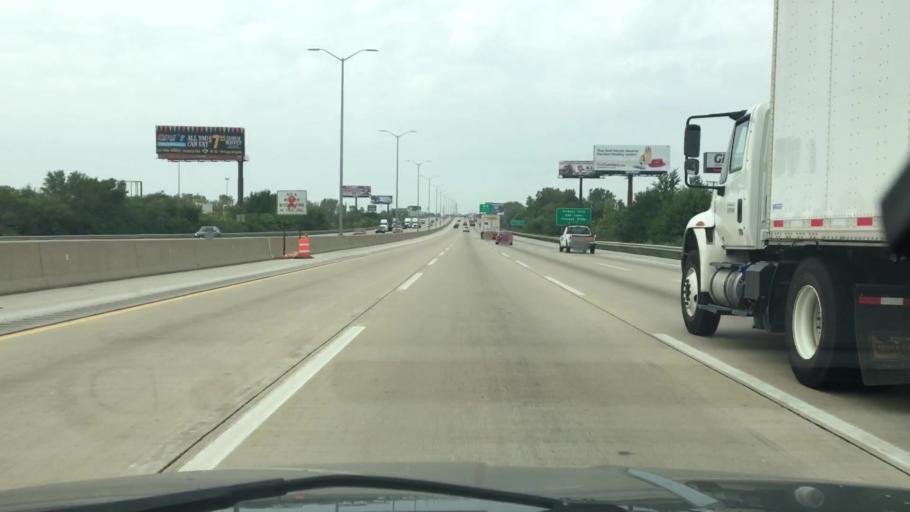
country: US
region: Illinois
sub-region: Cook County
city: Chicago Ridge
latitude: 41.7053
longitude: -87.7910
